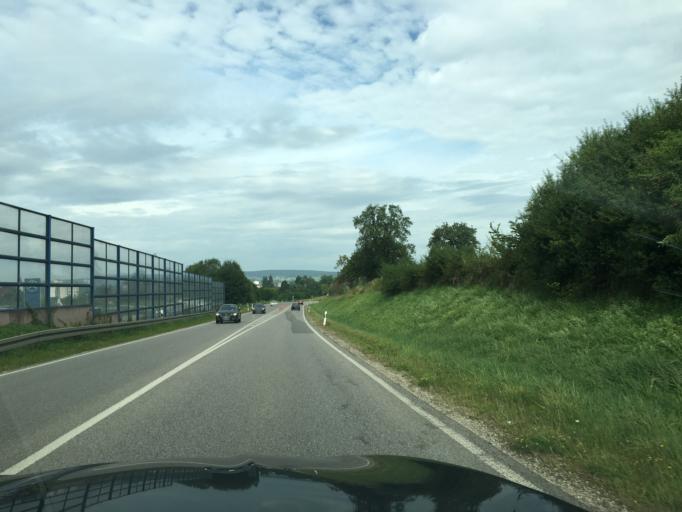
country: DE
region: Baden-Wuerttemberg
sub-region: Tuebingen Region
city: Ehingen
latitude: 48.2839
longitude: 9.7421
